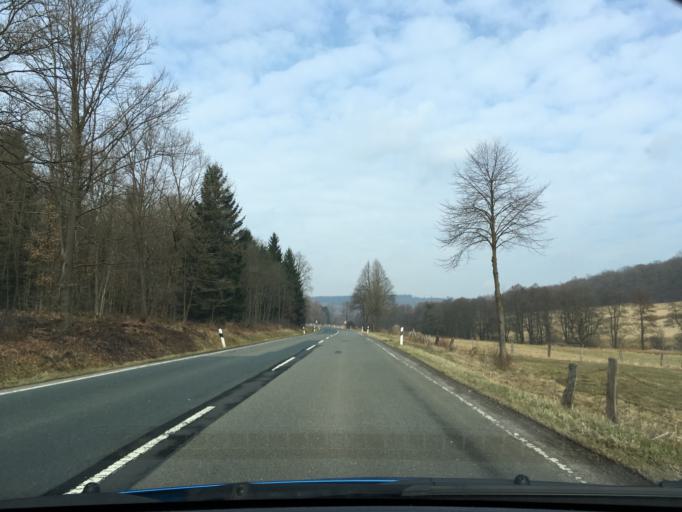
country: DE
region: Lower Saxony
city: Bodenfelde
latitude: 51.7186
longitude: 9.5237
